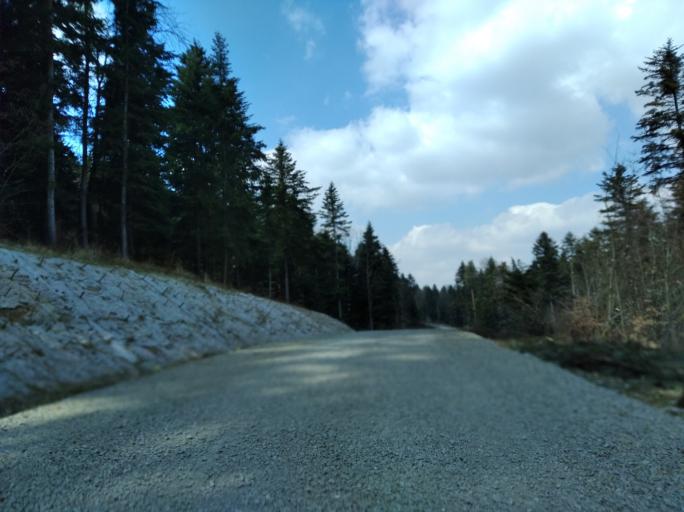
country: PL
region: Subcarpathian Voivodeship
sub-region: Powiat strzyzowski
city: Strzyzow
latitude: 49.8191
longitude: 21.8074
